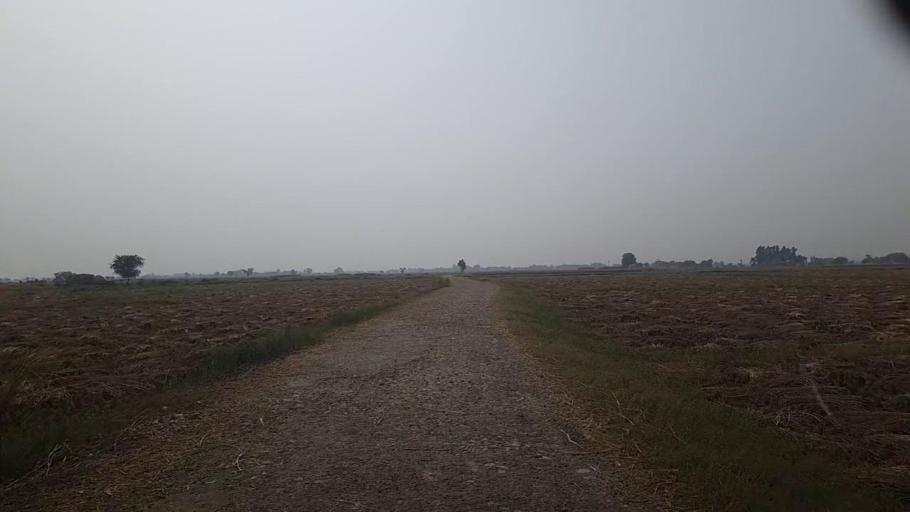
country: PK
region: Sindh
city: Kashmor
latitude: 28.3821
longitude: 69.4302
